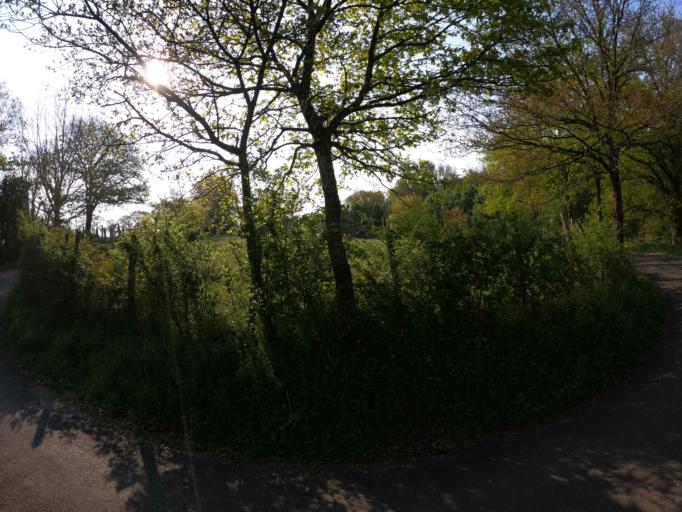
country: FR
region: Pays de la Loire
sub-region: Departement de Maine-et-Loire
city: La Romagne
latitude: 47.0685
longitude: -1.0094
